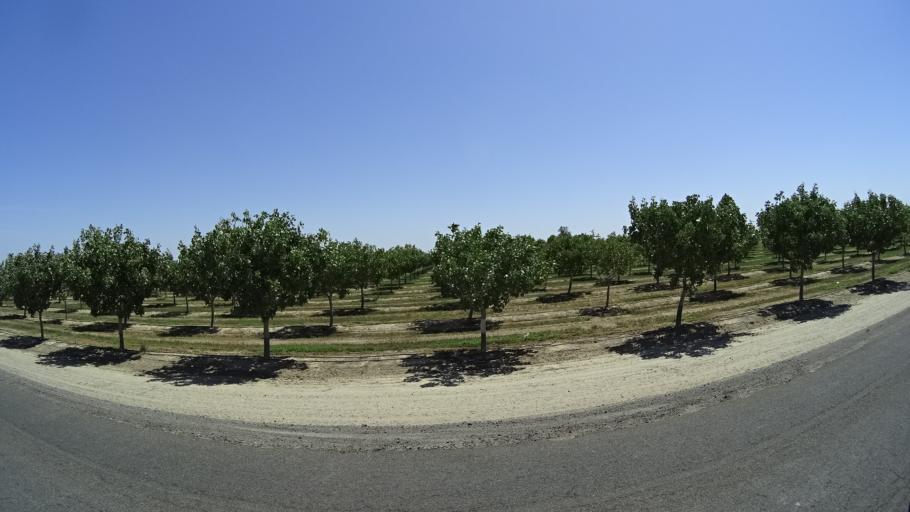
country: US
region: California
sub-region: Kings County
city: Lemoore
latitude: 36.2454
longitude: -119.7446
